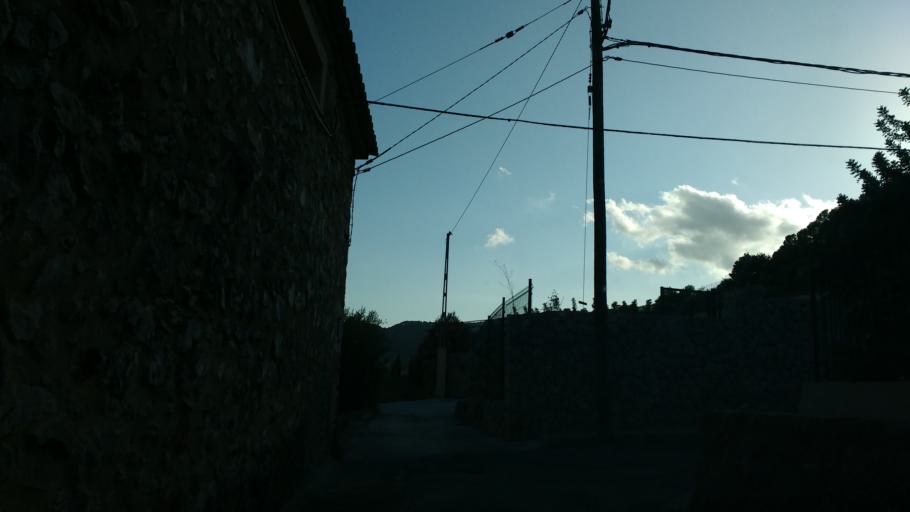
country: ES
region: Balearic Islands
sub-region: Illes Balears
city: Alaro
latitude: 39.7093
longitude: 2.7912
